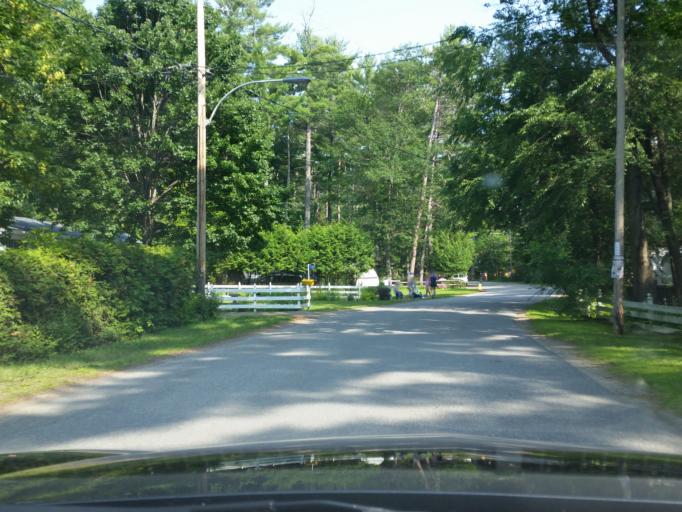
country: CA
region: Quebec
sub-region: Outaouais
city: Shawville
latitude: 45.5186
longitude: -76.4213
